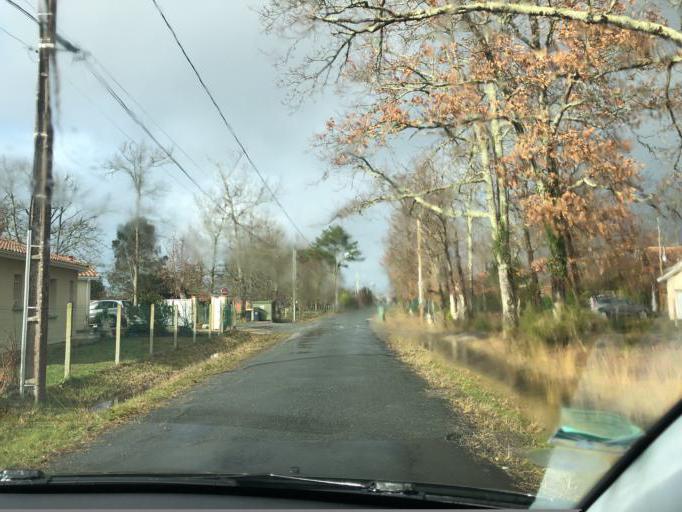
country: FR
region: Aquitaine
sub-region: Departement de la Gironde
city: Hourtin
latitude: 45.1803
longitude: -1.0535
